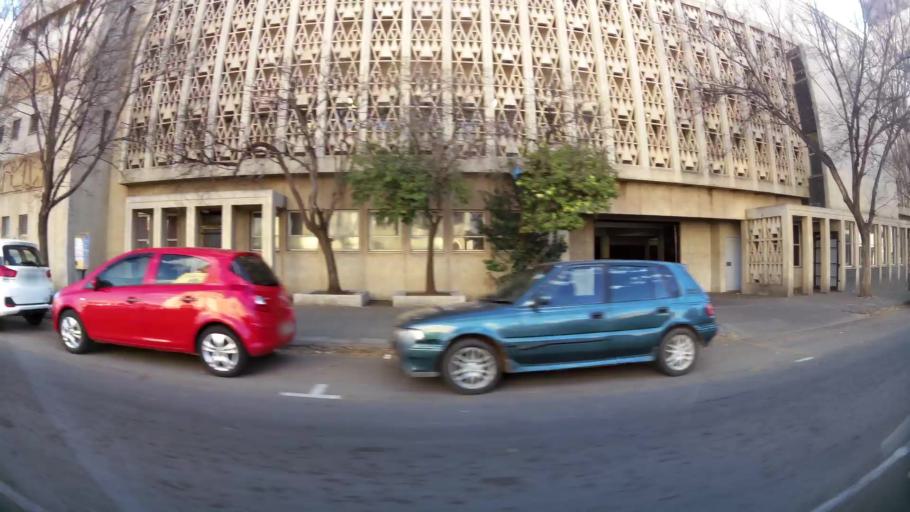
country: ZA
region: North-West
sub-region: Dr Kenneth Kaunda District Municipality
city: Klerksdorp
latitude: -26.8661
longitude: 26.6661
